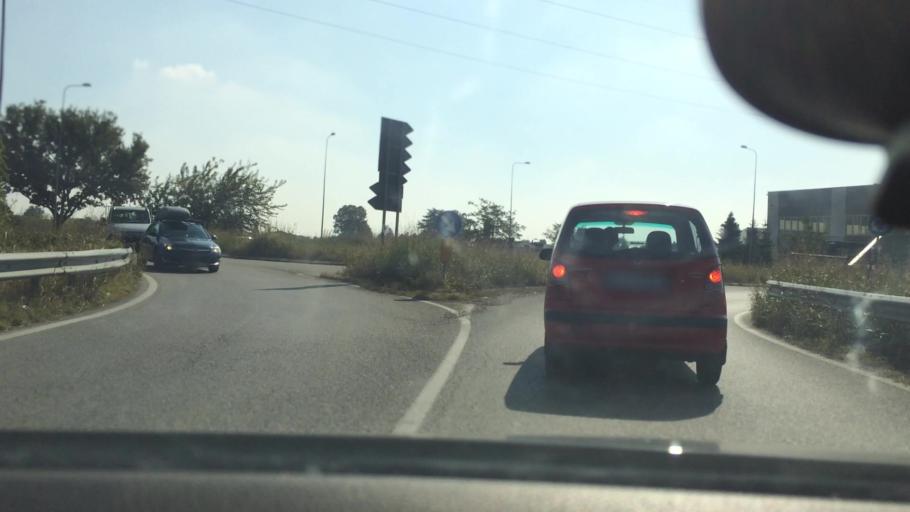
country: IT
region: Lombardy
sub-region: Citta metropolitana di Milano
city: Mesero
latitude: 45.5074
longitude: 8.8589
